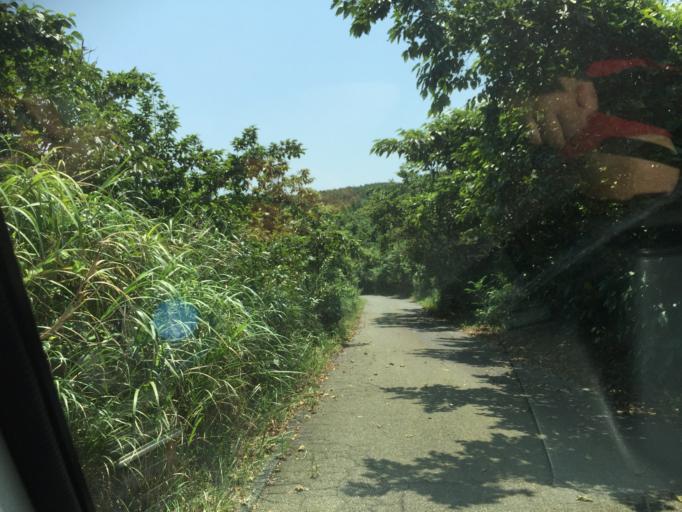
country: JP
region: Shizuoka
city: Shimoda
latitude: 34.0999
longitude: 139.5472
